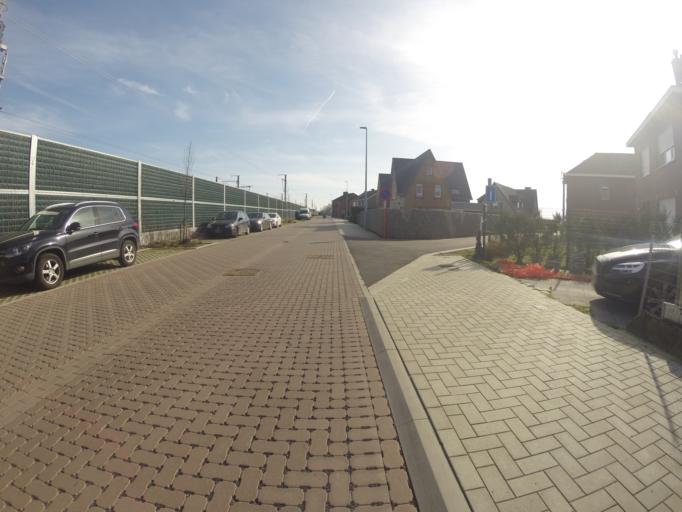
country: BE
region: Flanders
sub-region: Provincie West-Vlaanderen
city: Oostkamp
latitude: 51.1533
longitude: 3.2594
